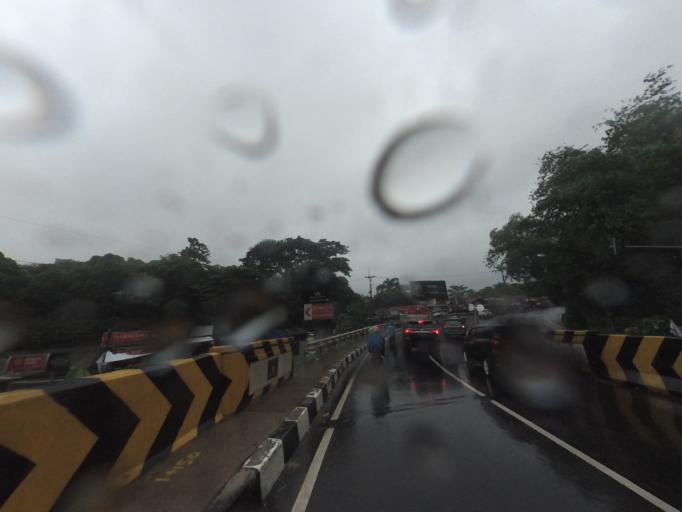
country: ID
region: West Java
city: Caringin
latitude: -6.6527
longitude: 106.8688
